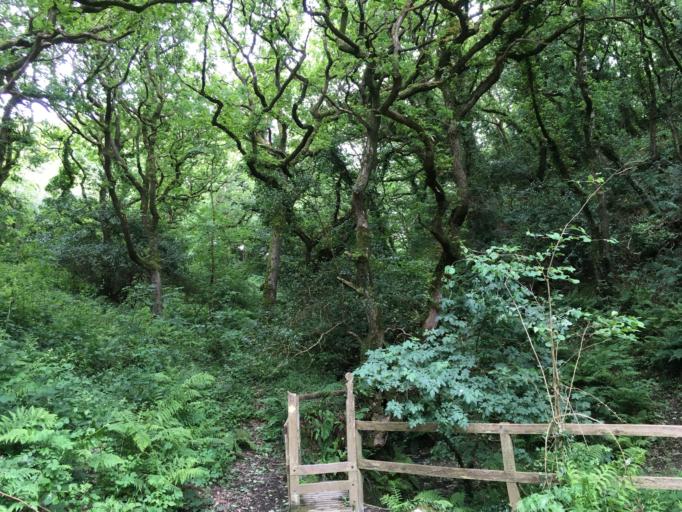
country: GB
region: England
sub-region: Cornwall
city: Poundstock
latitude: 50.7625
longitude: -4.5909
